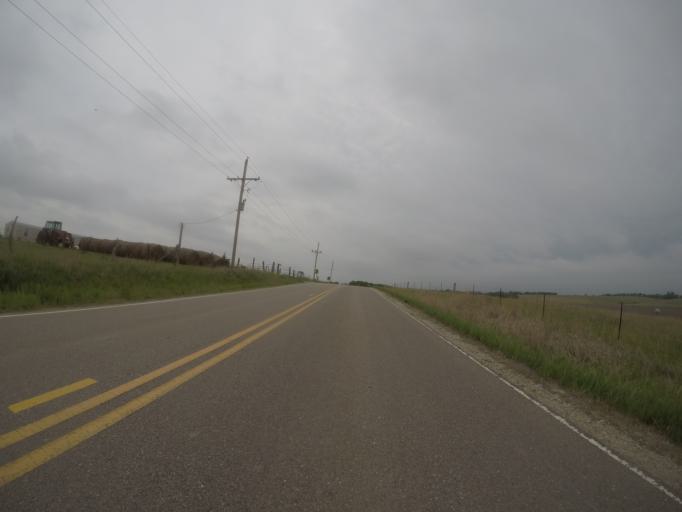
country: US
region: Kansas
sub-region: Pottawatomie County
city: Westmoreland
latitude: 39.5222
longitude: -96.2410
